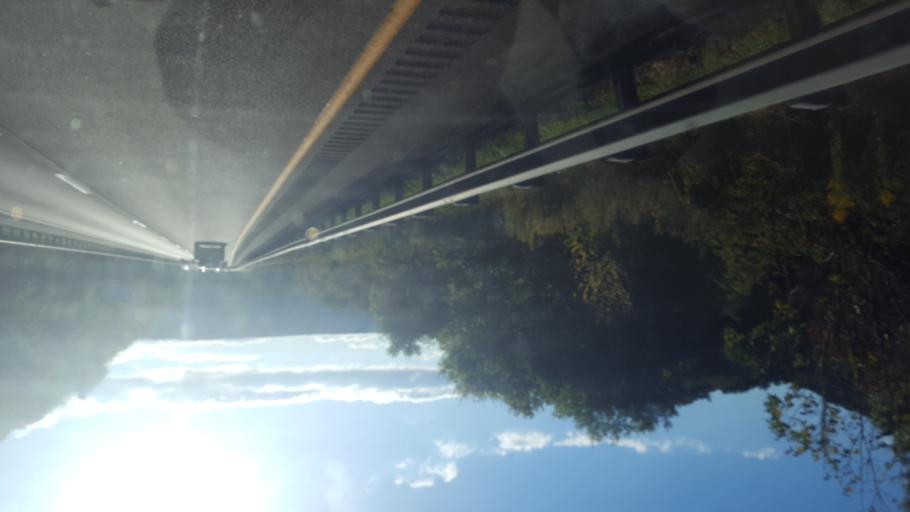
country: US
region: Maryland
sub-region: Allegany County
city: La Vale
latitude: 39.6378
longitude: -78.8578
